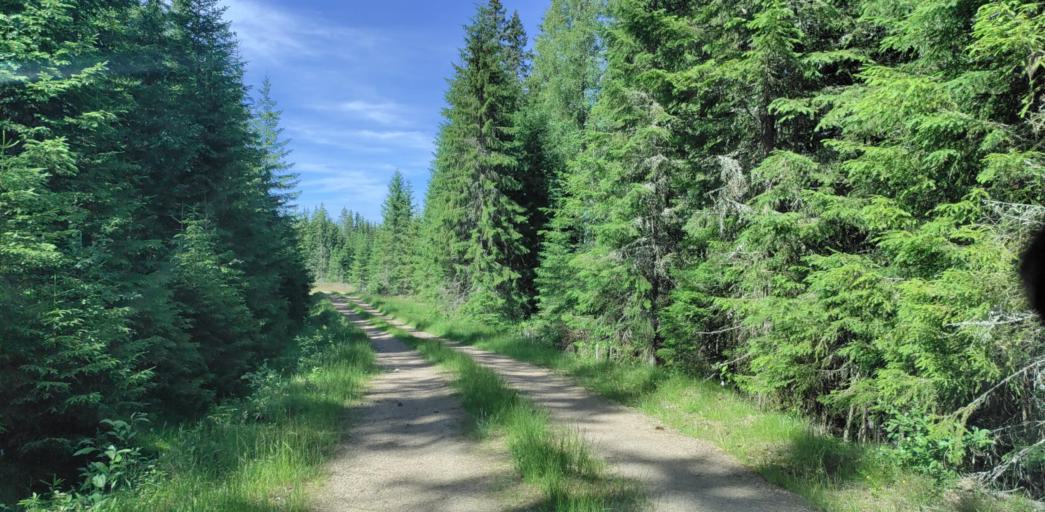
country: SE
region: Vaermland
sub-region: Hagfors Kommun
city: Ekshaerad
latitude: 60.0922
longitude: 13.3765
